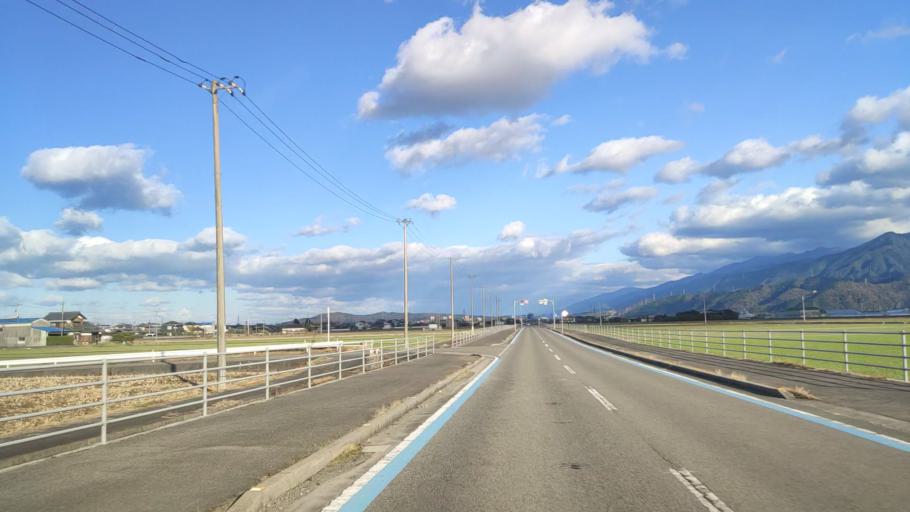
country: JP
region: Ehime
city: Saijo
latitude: 33.9074
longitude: 133.1467
